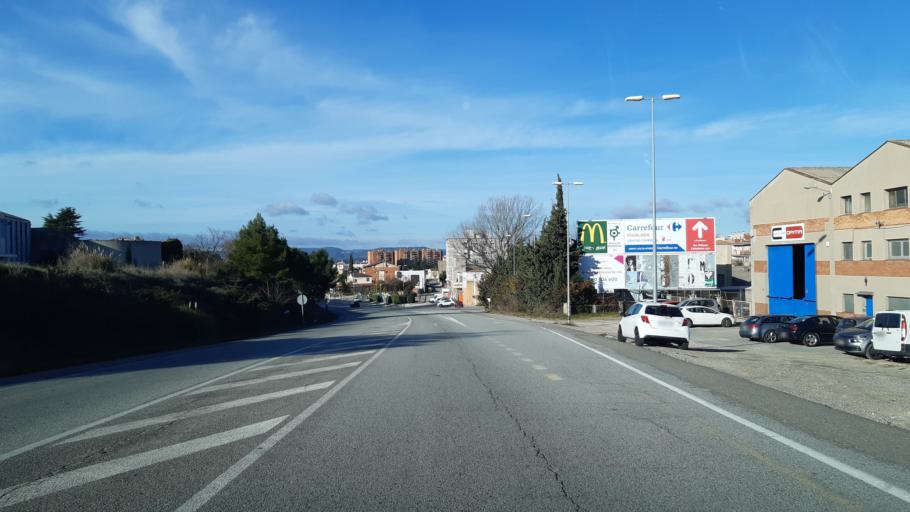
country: ES
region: Catalonia
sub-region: Provincia de Barcelona
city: Vilanova del Cami
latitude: 41.5786
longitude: 1.6440
